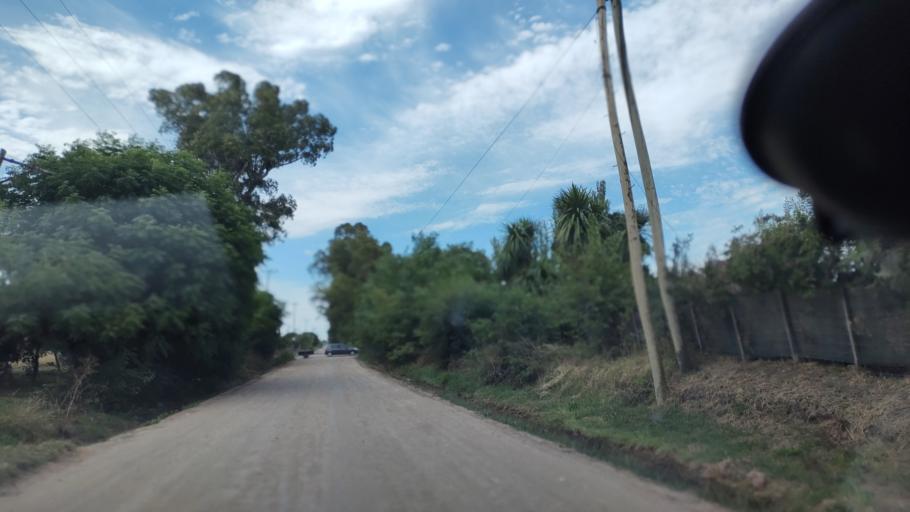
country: AR
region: Buenos Aires
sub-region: Partido de Lobos
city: Lobos
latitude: -35.1727
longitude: -59.1086
